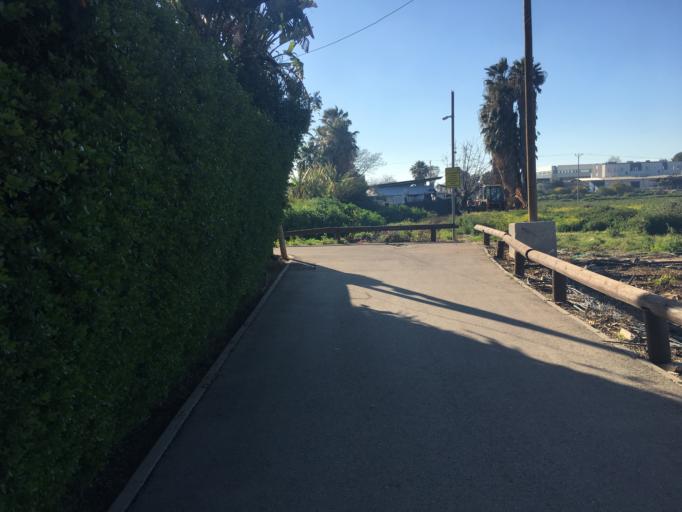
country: IL
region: Tel Aviv
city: Ramat HaSharon
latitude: 32.1420
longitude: 34.8241
